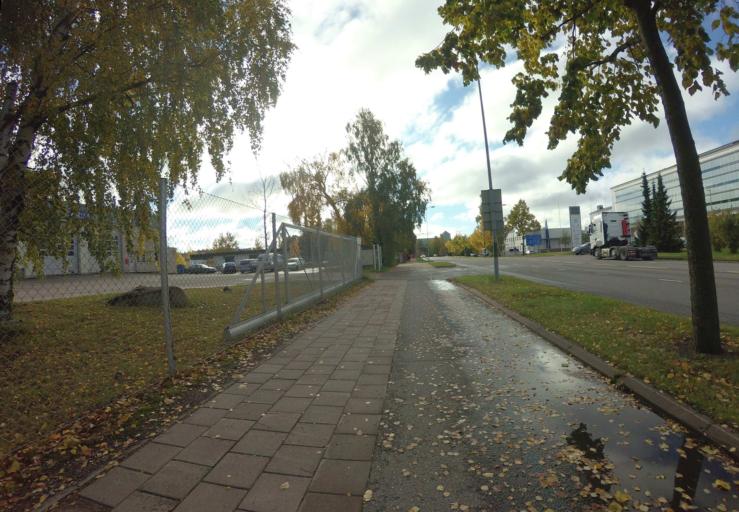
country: FI
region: Varsinais-Suomi
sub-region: Turku
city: Turku
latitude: 60.4403
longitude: 22.2284
